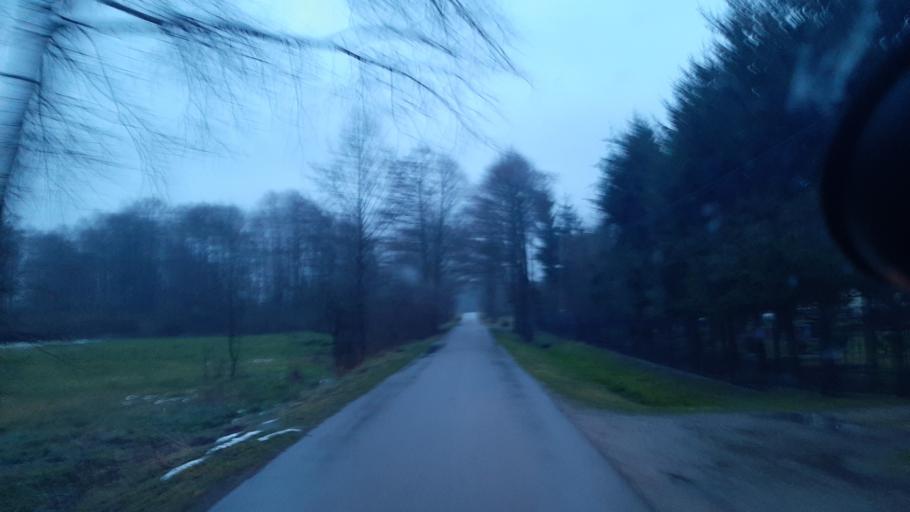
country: PL
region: Lublin Voivodeship
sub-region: Powiat lubelski
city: Jastkow
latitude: 51.3885
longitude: 22.4136
